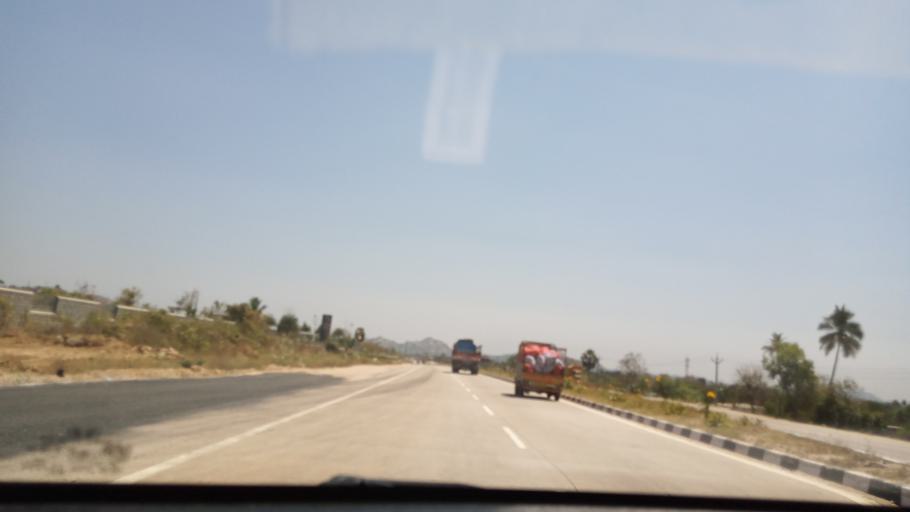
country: IN
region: Andhra Pradesh
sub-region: Chittoor
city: Chittoor
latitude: 13.1940
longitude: 79.0303
